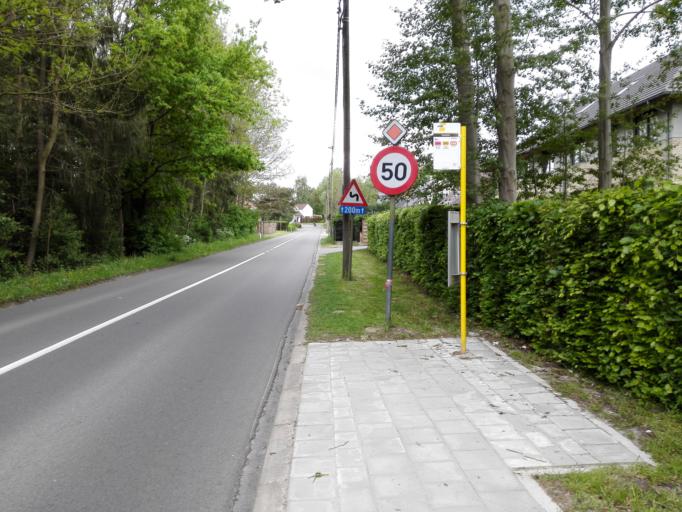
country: BE
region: Flanders
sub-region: Provincie Vlaams-Brabant
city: Huldenberg
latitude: 50.8010
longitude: 4.6021
